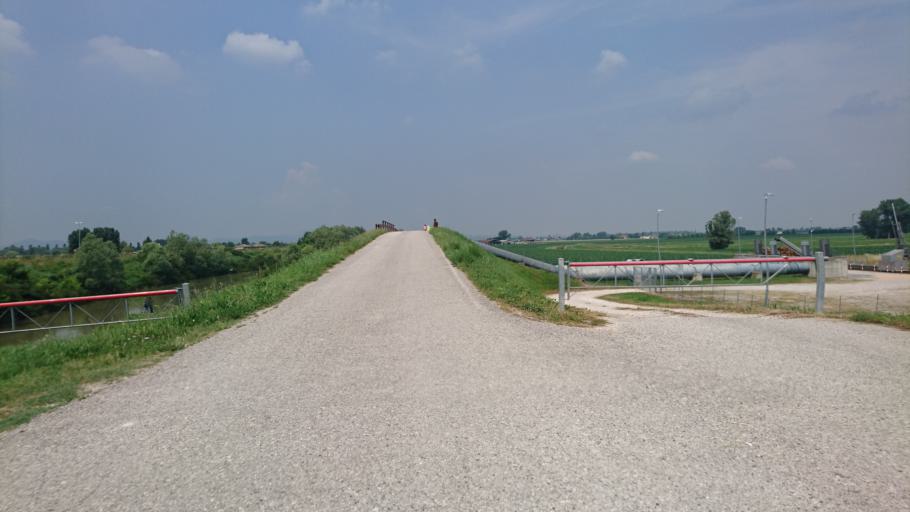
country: IT
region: Veneto
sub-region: Provincia di Padova
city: Bovolenta
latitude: 45.2728
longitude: 11.9235
